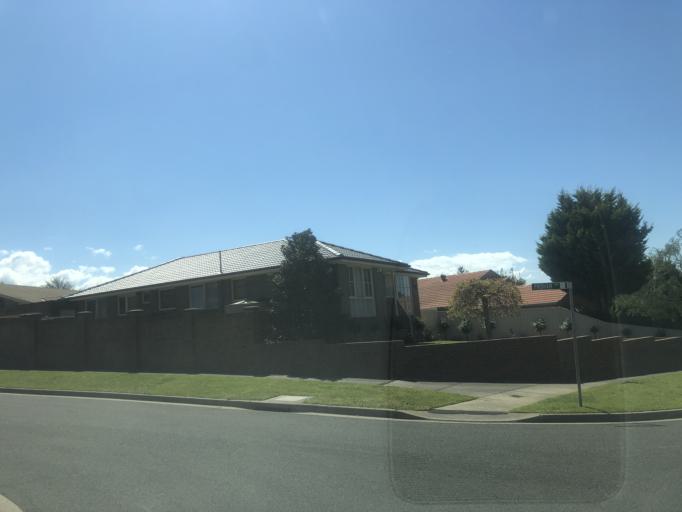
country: AU
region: Victoria
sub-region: Casey
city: Endeavour Hills
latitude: -37.9870
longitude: 145.2704
